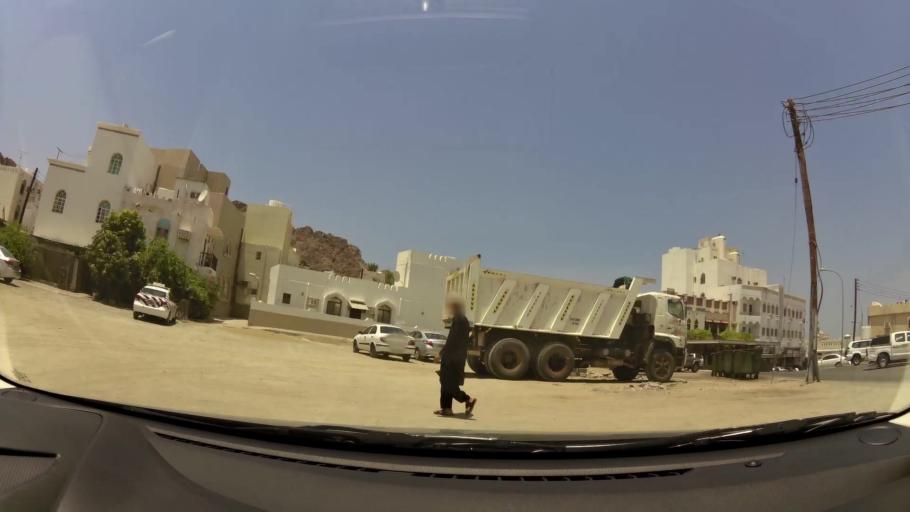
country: OM
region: Muhafazat Masqat
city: Muscat
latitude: 23.6252
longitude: 58.5605
